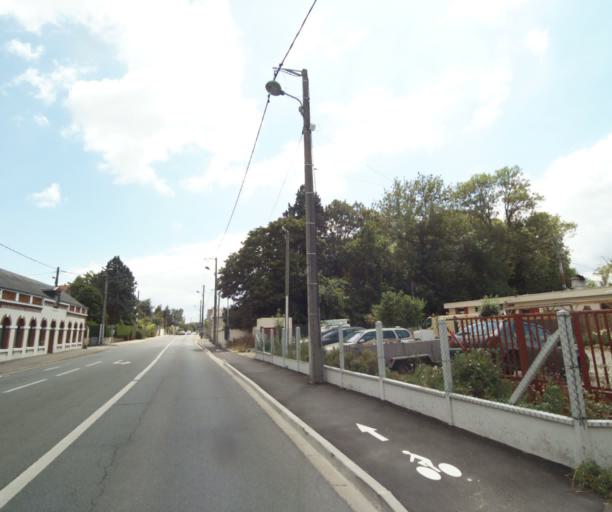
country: FR
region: Centre
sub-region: Departement du Loiret
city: Saint-Jean-de-Braye
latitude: 47.9072
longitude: 1.9824
